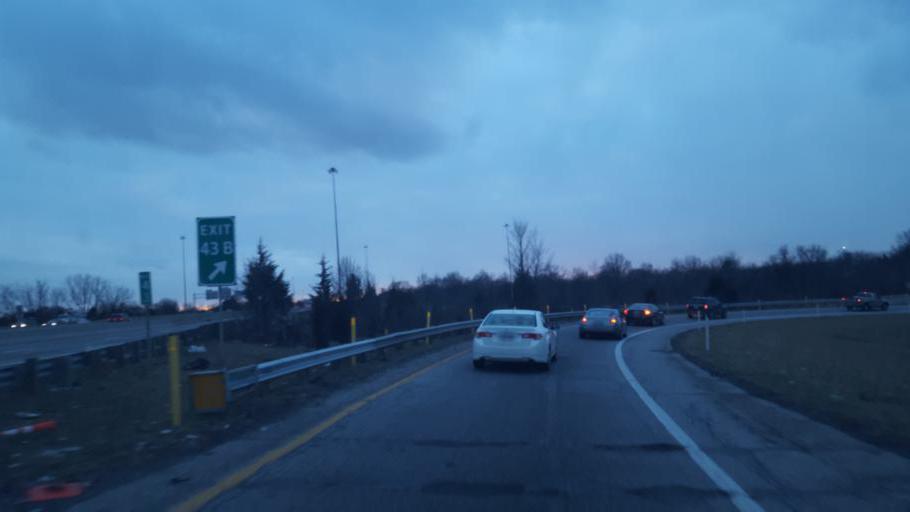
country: US
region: Ohio
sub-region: Franklin County
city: Blacklick Estates
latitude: 39.9329
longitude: -82.8548
